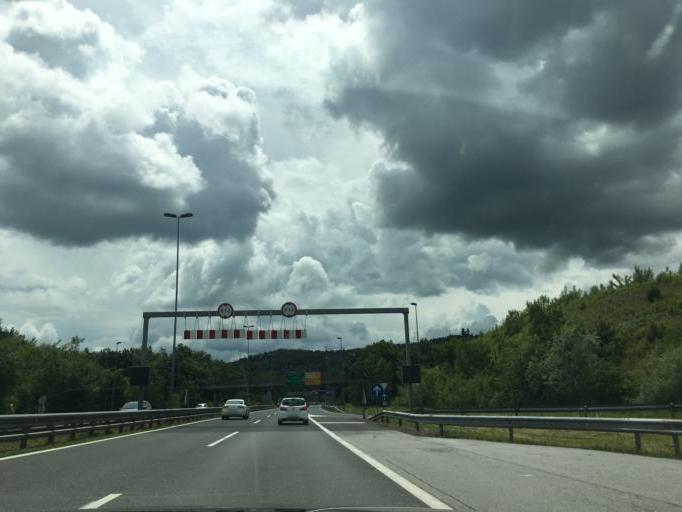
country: SI
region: Medvode
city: Zgornje Pirnice
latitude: 46.1061
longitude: 14.4699
